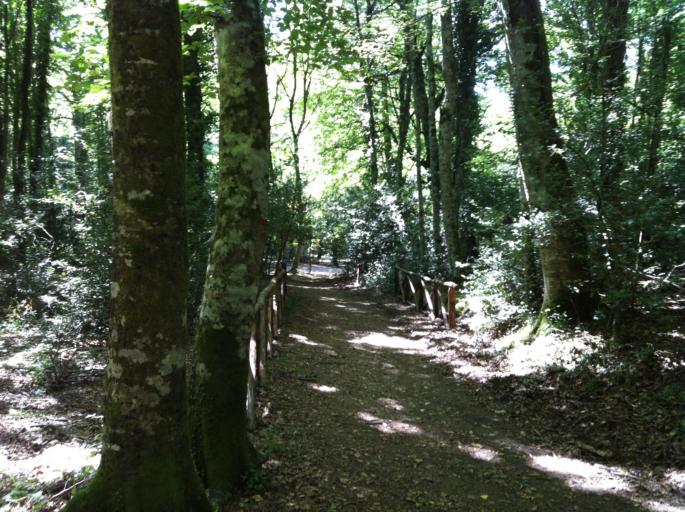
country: IT
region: Apulia
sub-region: Provincia di Foggia
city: Vico del Gargano
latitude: 41.8121
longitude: 15.9886
